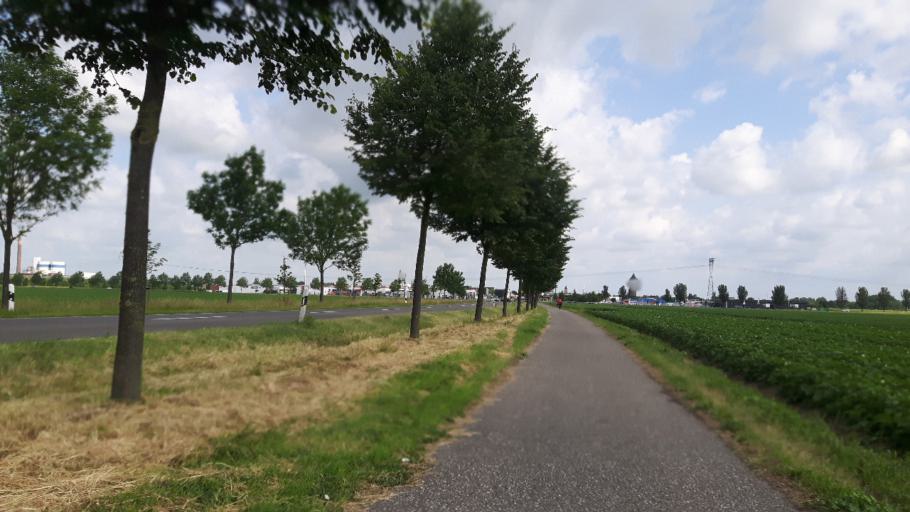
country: DE
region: Saxony
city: Dobernitz
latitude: 51.5071
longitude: 12.3389
